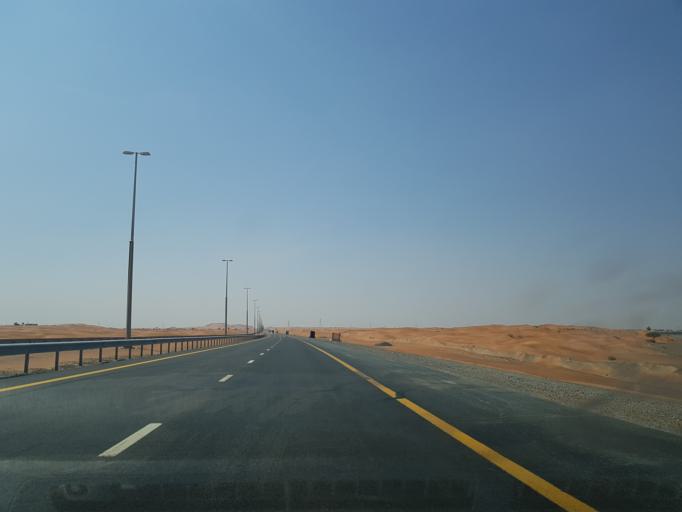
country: AE
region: Ash Shariqah
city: Adh Dhayd
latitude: 25.2400
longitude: 55.8860
